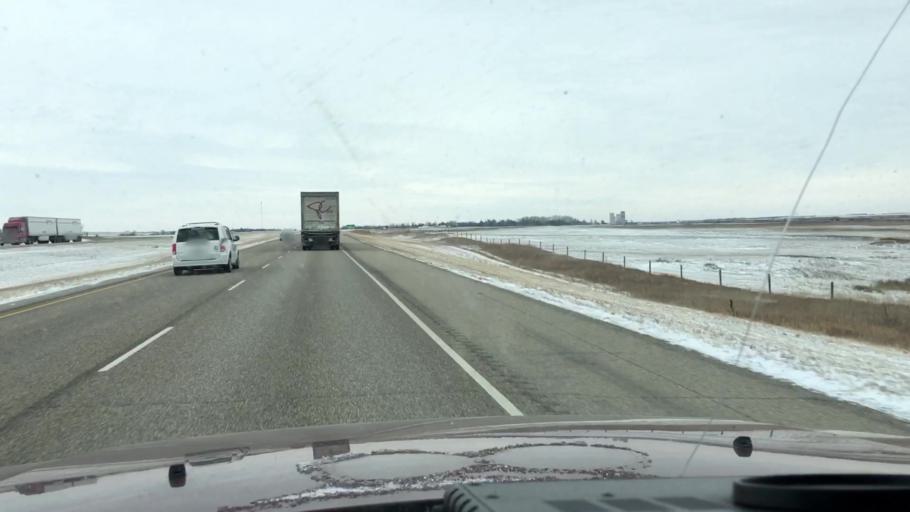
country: CA
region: Saskatchewan
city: Saskatoon
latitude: 51.5201
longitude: -106.2936
